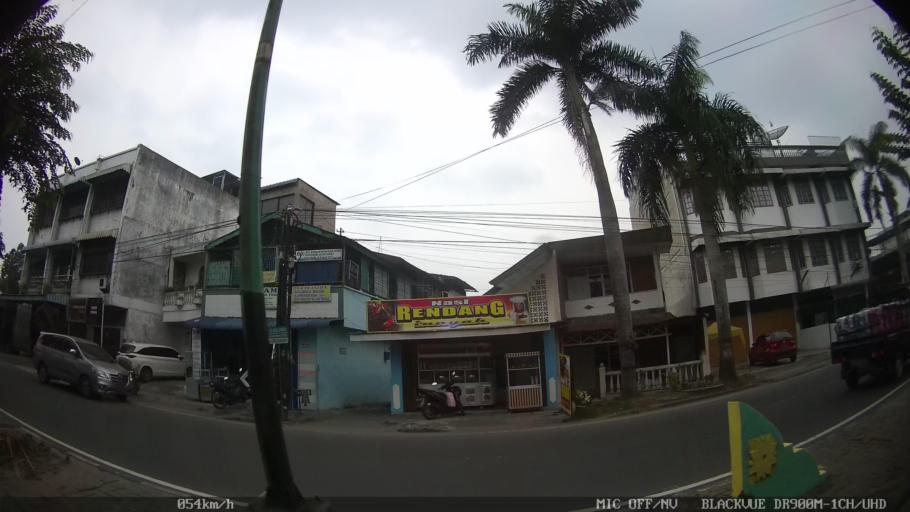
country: ID
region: North Sumatra
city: Medan
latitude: 3.5669
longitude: 98.6881
